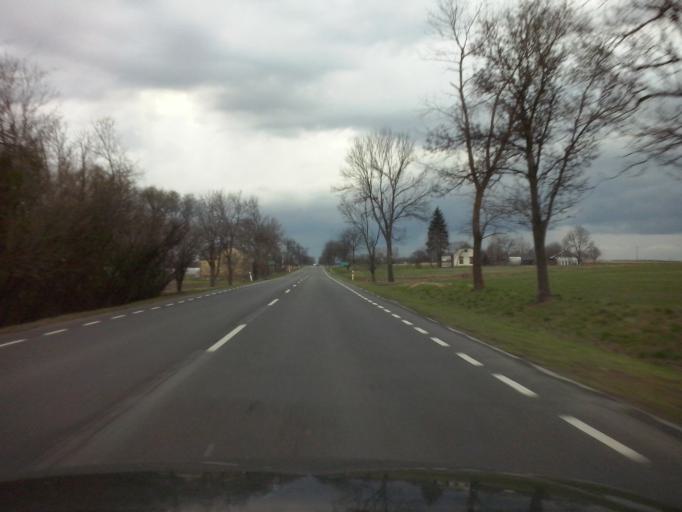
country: PL
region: Lublin Voivodeship
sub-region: Powiat chelmski
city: Rejowiec Fabryczny
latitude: 51.1710
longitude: 23.3090
